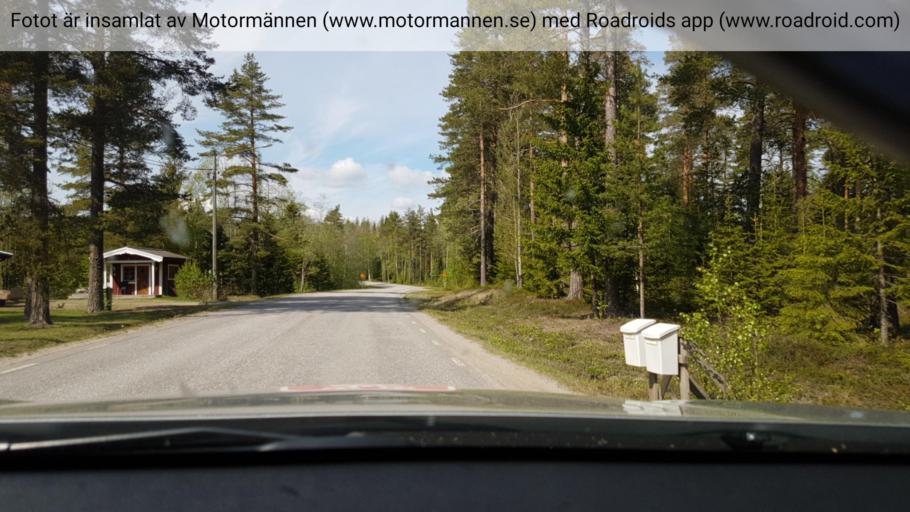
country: SE
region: Vaesterbotten
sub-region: Umea Kommun
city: Roback
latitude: 63.8382
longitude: 20.0983
